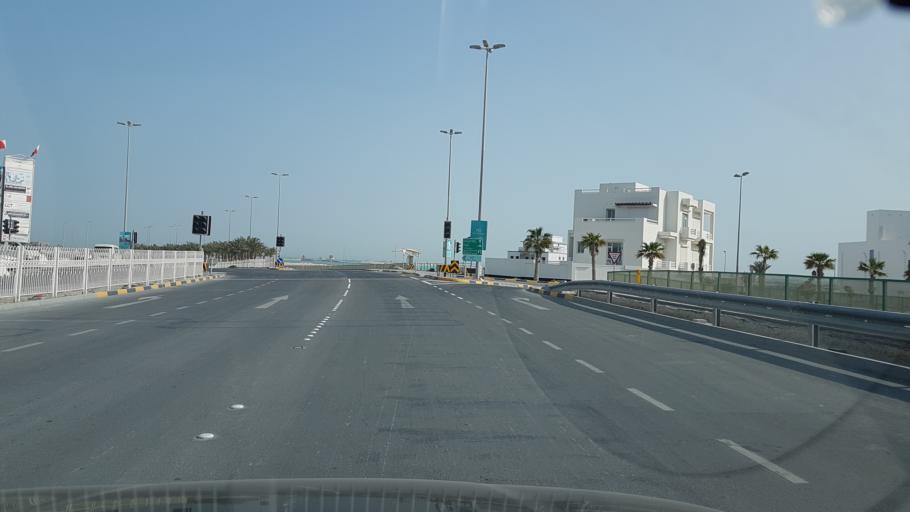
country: BH
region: Muharraq
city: Al Hadd
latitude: 26.2693
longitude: 50.6707
